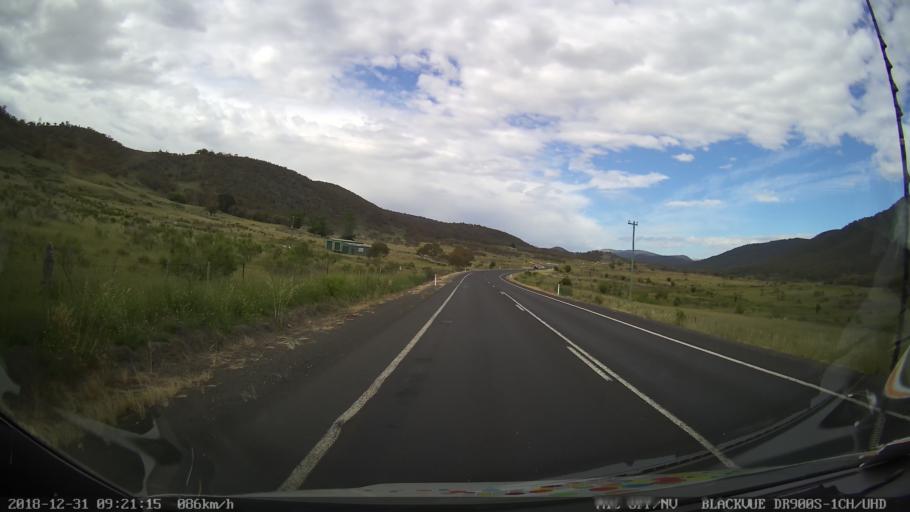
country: AU
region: New South Wales
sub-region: Snowy River
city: Jindabyne
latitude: -36.4271
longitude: 148.5641
